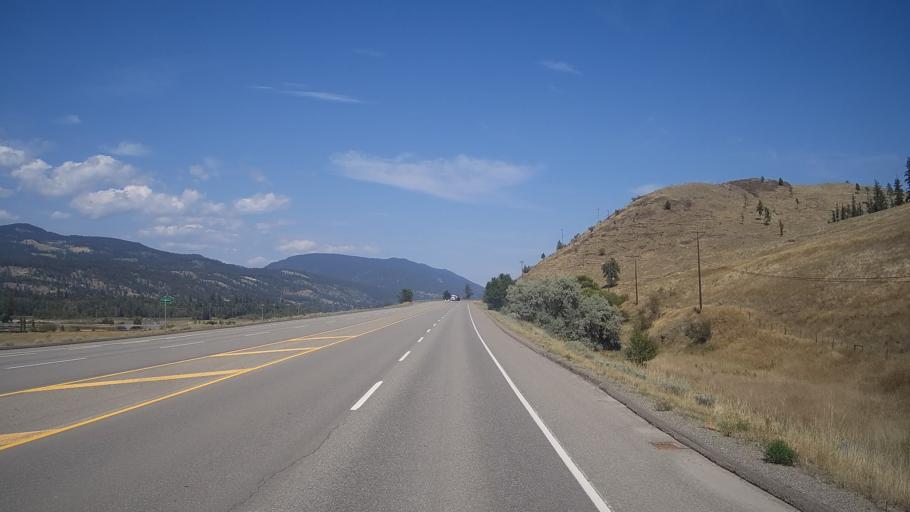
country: CA
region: British Columbia
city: Kamloops
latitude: 50.8211
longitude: -120.2912
